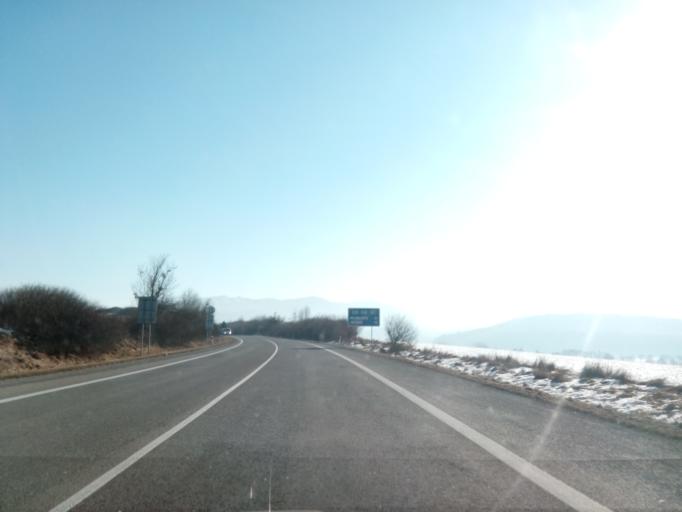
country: SK
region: Kosicky
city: Kosice
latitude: 48.7297
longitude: 21.4406
